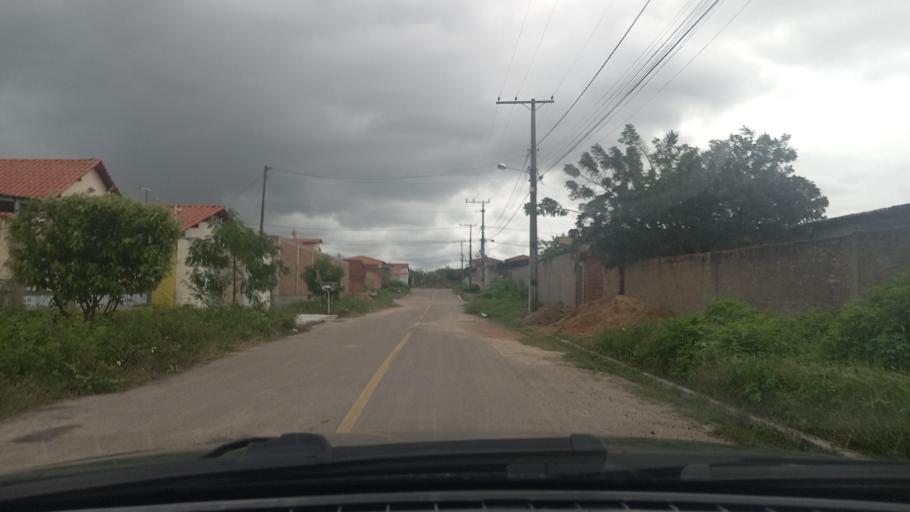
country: BR
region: Bahia
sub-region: Paulo Afonso
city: Paulo Afonso
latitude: -9.3999
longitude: -38.2437
